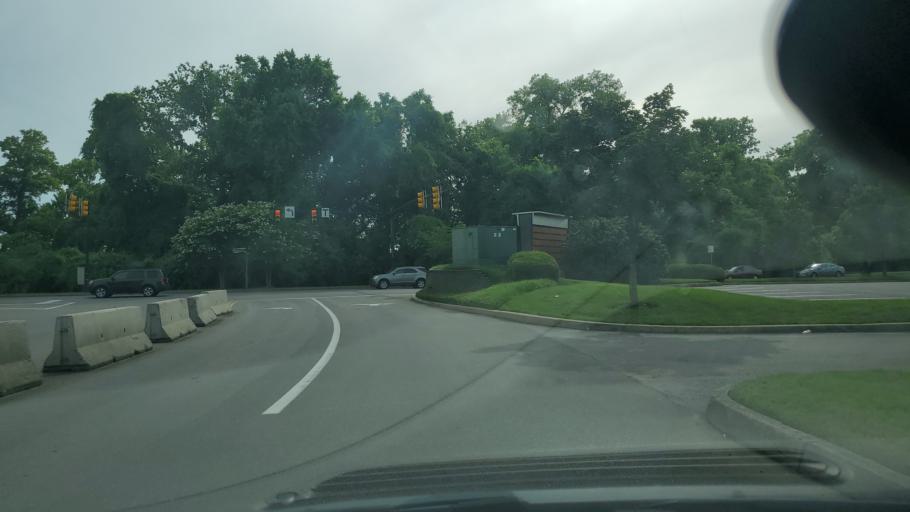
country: US
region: Tennessee
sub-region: Davidson County
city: Lakewood
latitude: 36.1979
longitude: -86.6911
